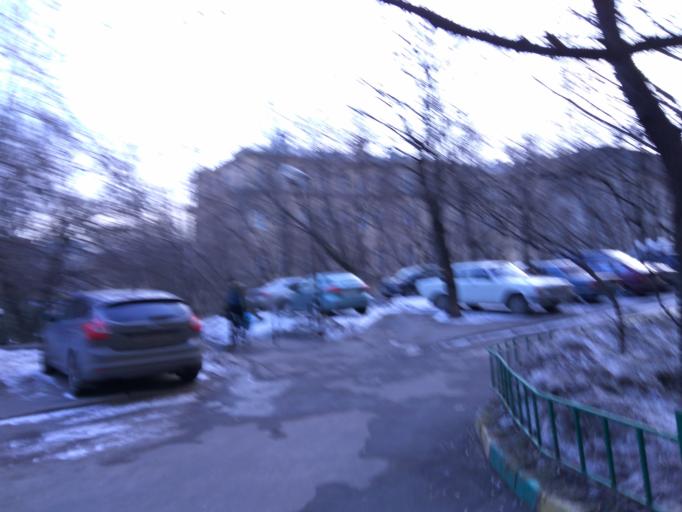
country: RU
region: Moscow
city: Moscow
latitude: 55.7750
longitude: 37.6248
